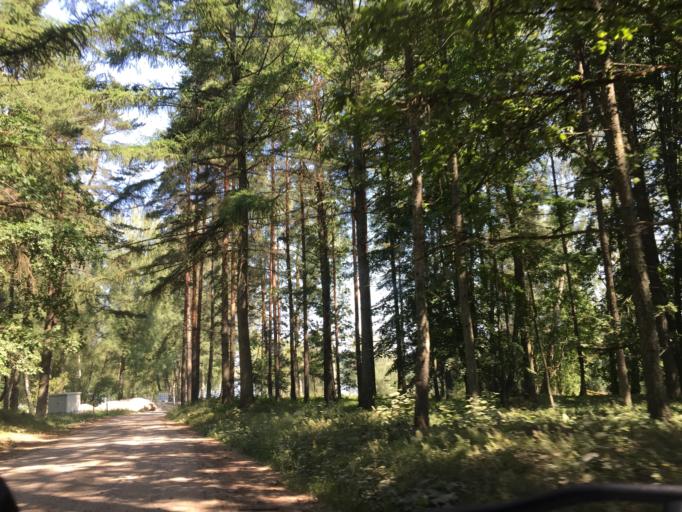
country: LV
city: Tervete
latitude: 56.4932
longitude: 23.4056
